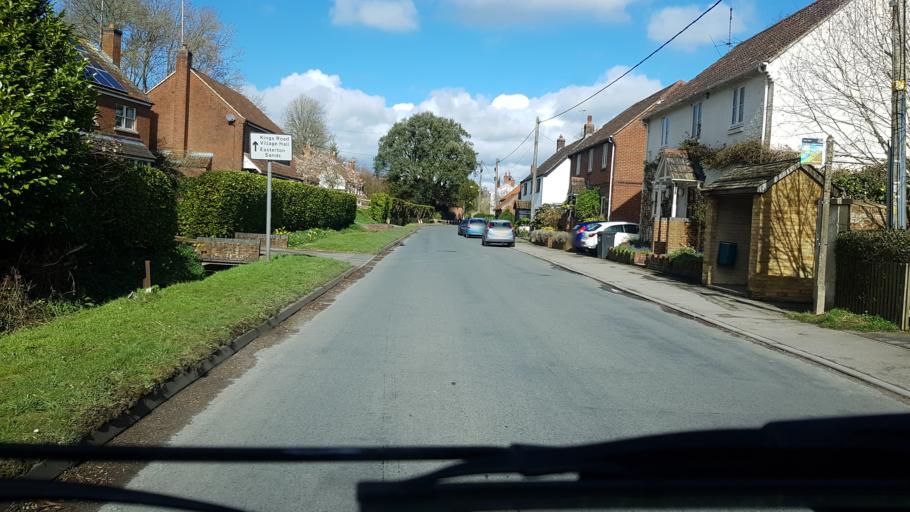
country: GB
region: England
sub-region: Wiltshire
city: Market Lavington
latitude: 51.2934
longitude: -1.9714
